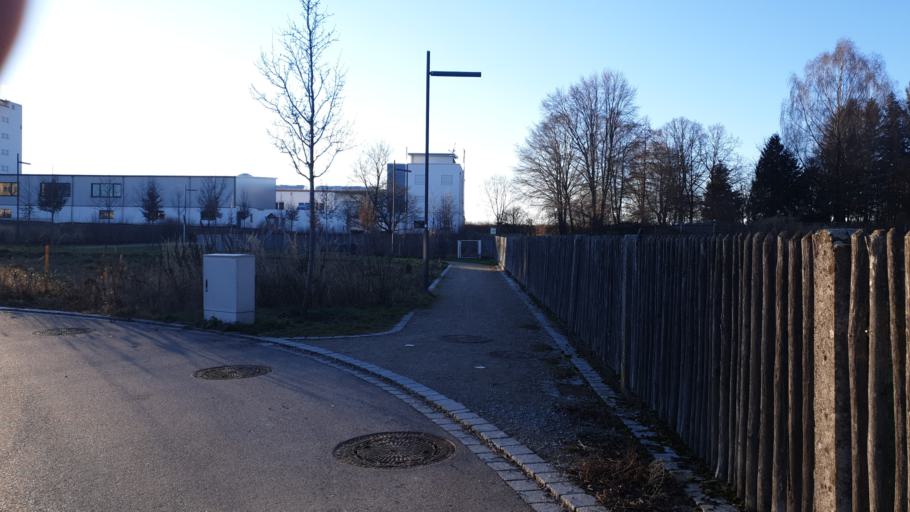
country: DE
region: Bavaria
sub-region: Upper Bavaria
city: Markt Schwaben
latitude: 48.1966
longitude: 11.8590
